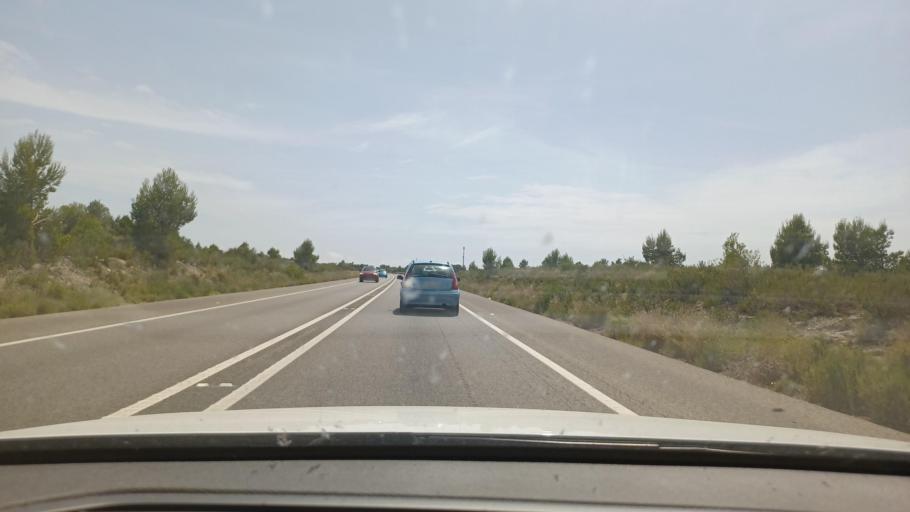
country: ES
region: Catalonia
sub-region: Provincia de Tarragona
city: l'Ametlla de Mar
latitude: 40.9153
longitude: 0.8164
